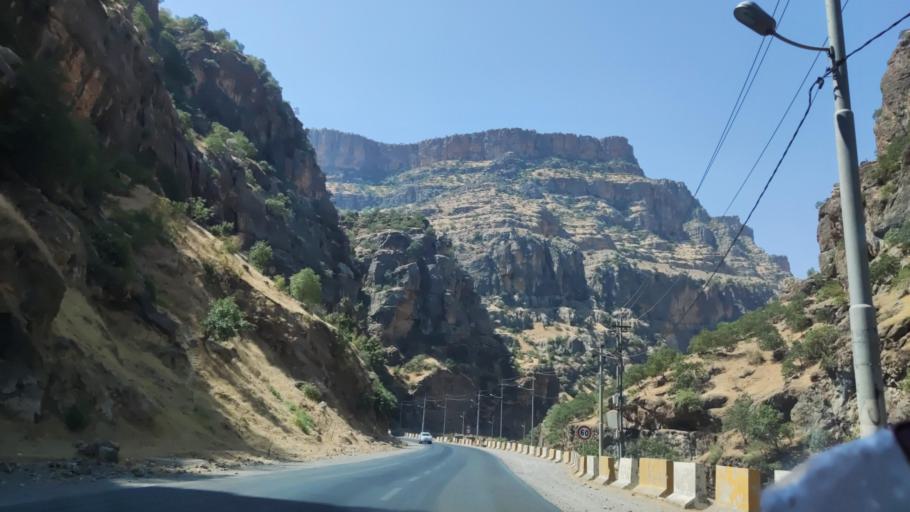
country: IQ
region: Arbil
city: Ruwandiz
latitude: 36.6339
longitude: 44.4908
